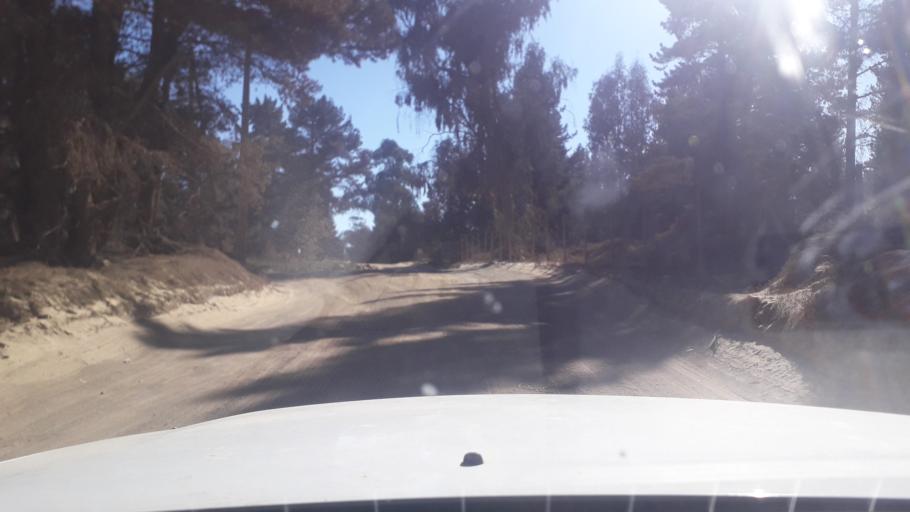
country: CL
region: Valparaiso
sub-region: Provincia de Valparaiso
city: Vina del Mar
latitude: -32.9562
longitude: -71.5210
